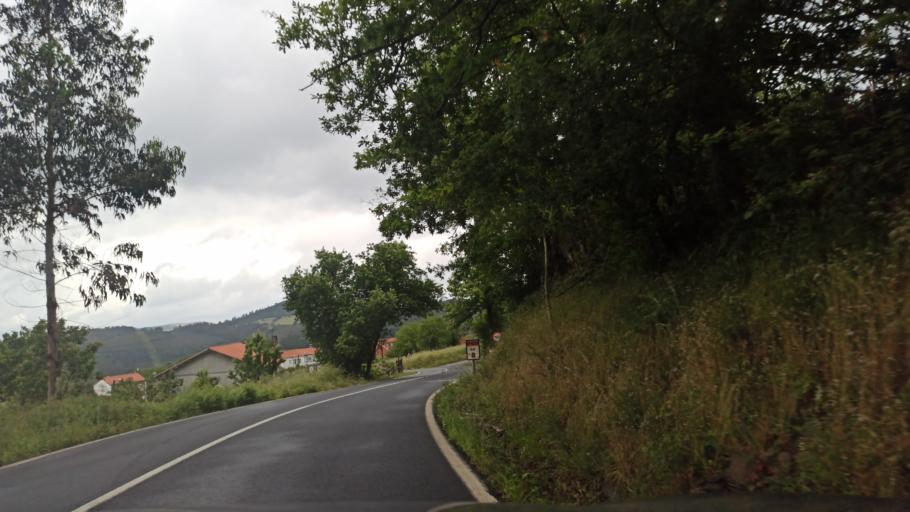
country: ES
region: Galicia
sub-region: Provincia da Coruna
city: Santiso
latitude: 42.7854
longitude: -8.0805
